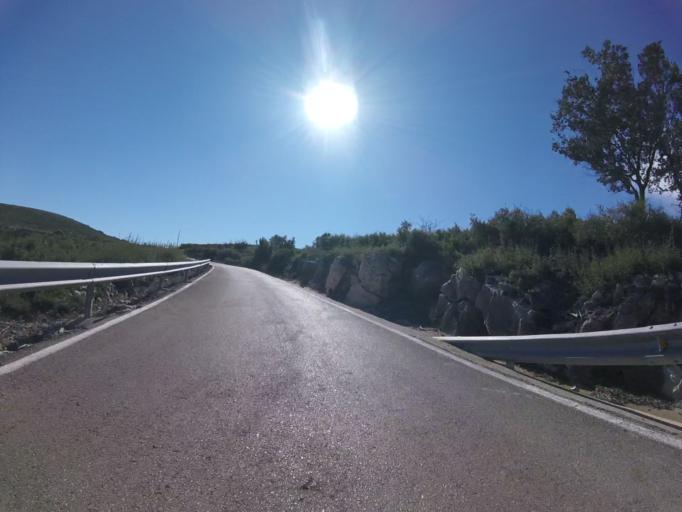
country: ES
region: Valencia
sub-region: Provincia de Castello
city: Albocasser
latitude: 40.3752
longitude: 0.0185
